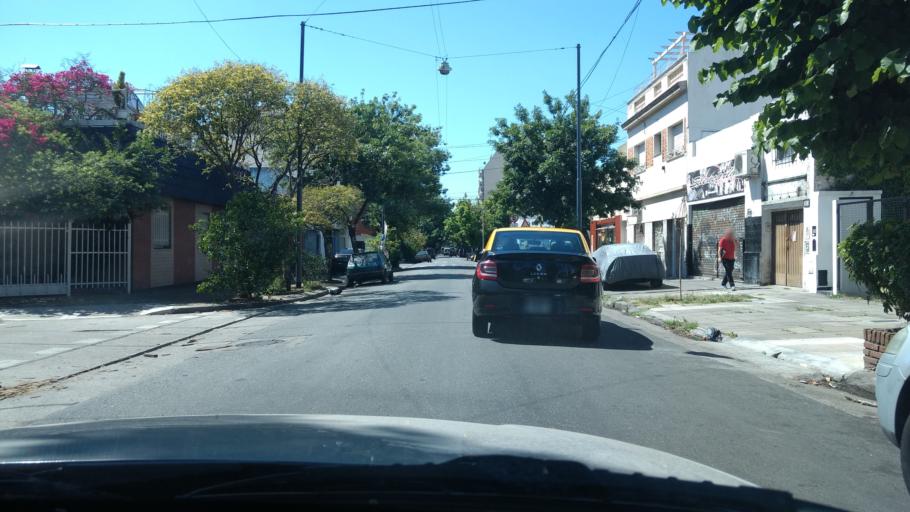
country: AR
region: Buenos Aires F.D.
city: Villa Santa Rita
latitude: -34.6136
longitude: -58.5068
